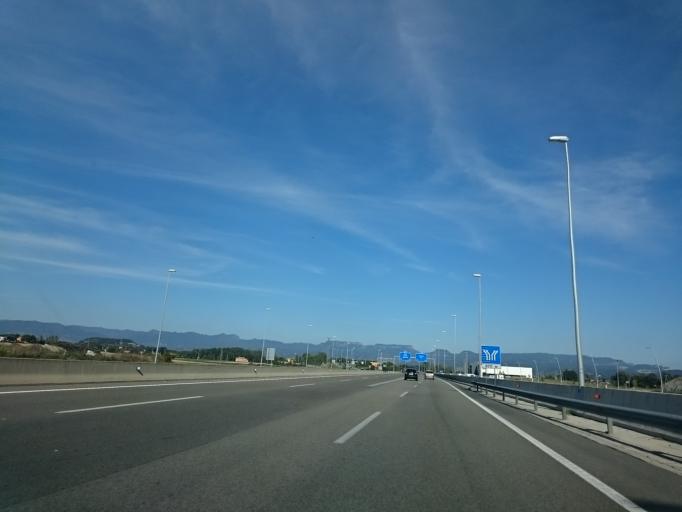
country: ES
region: Catalonia
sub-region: Provincia de Barcelona
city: Gurb
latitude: 41.9539
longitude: 2.2404
